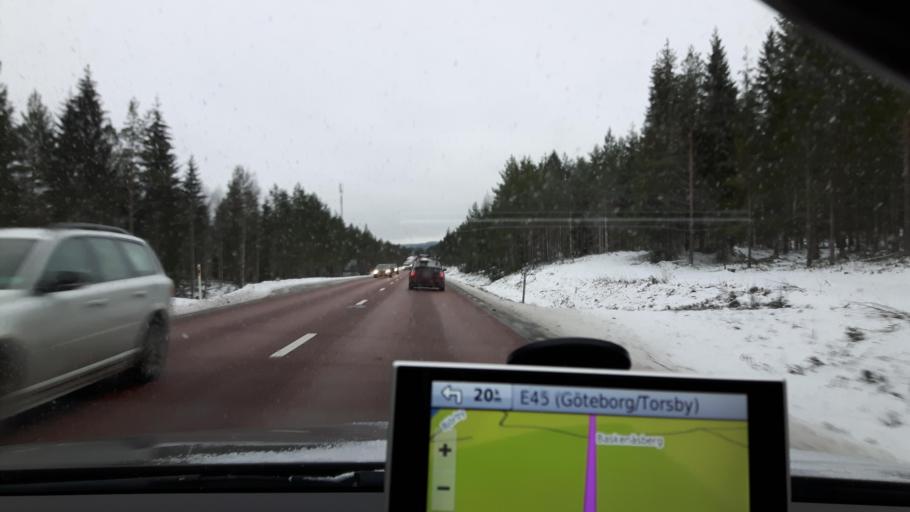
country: SE
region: Vaermland
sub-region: Hagfors Kommun
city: Ekshaerad
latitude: 60.4075
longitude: 13.2578
